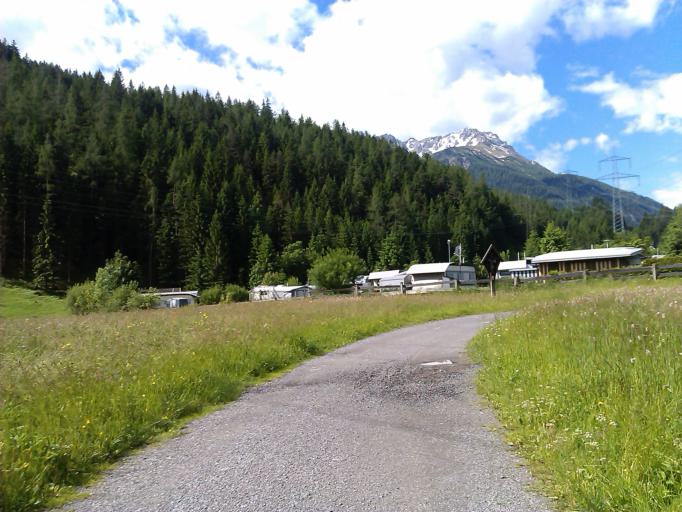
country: AT
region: Tyrol
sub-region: Politischer Bezirk Reutte
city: Biberwier
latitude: 47.3826
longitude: 10.9035
